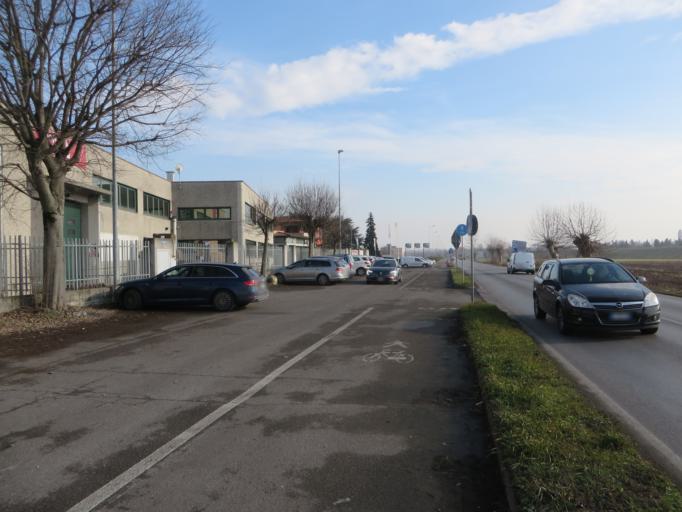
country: IT
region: Lombardy
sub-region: Provincia di Brescia
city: Torbole Casaglia
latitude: 45.5166
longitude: 10.1098
